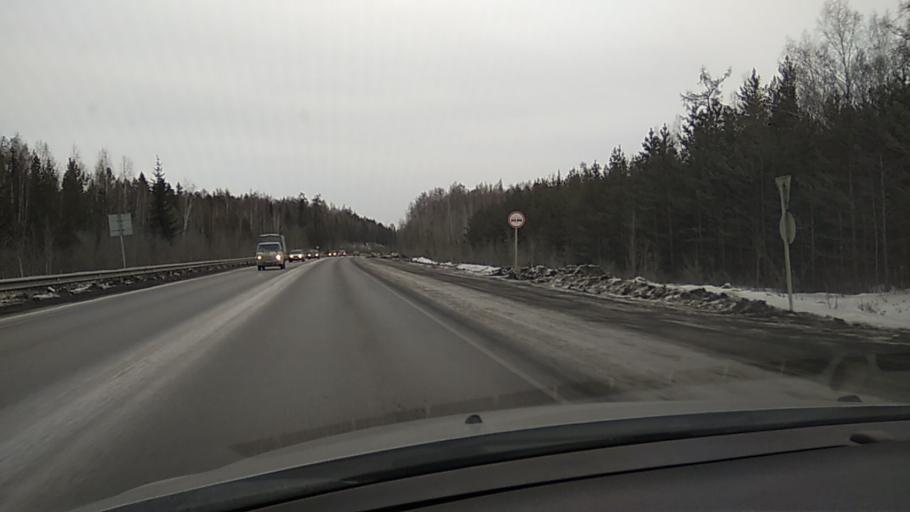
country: RU
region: Sverdlovsk
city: Talitsa
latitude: 56.8362
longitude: 60.0002
